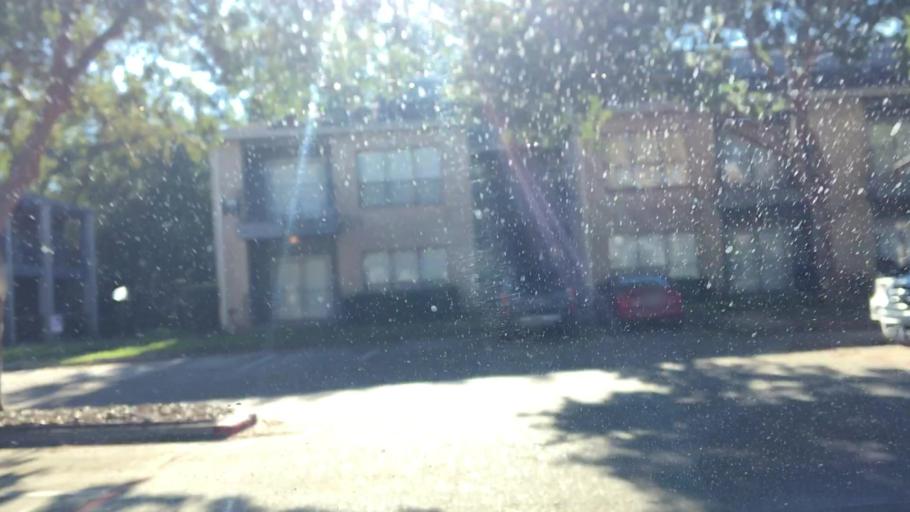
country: US
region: Texas
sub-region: Harris County
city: Nassau Bay
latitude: 29.5357
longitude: -95.1016
